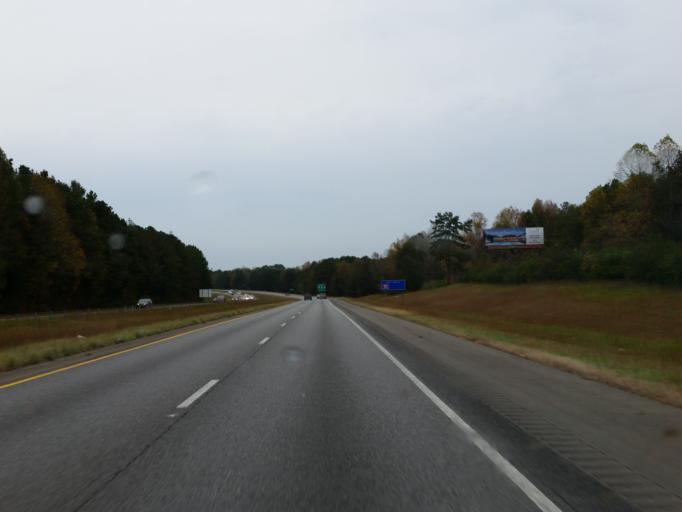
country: US
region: Georgia
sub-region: Cherokee County
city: Holly Springs
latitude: 34.1982
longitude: -84.5003
